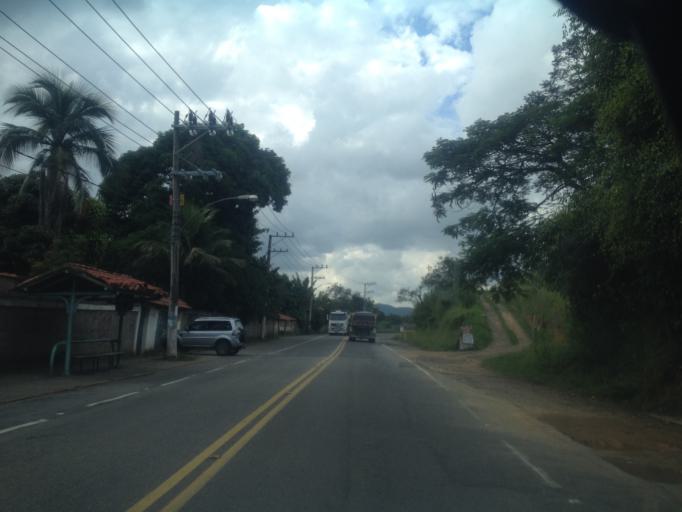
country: BR
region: Rio de Janeiro
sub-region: Porto Real
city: Porto Real
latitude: -22.4249
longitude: -44.2823
